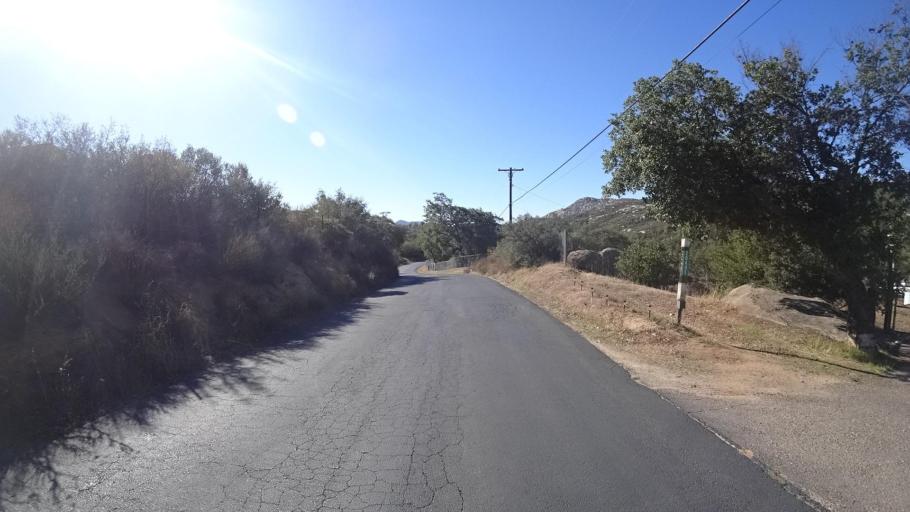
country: MX
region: Baja California
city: Tecate
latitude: 32.6686
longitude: -116.7080
